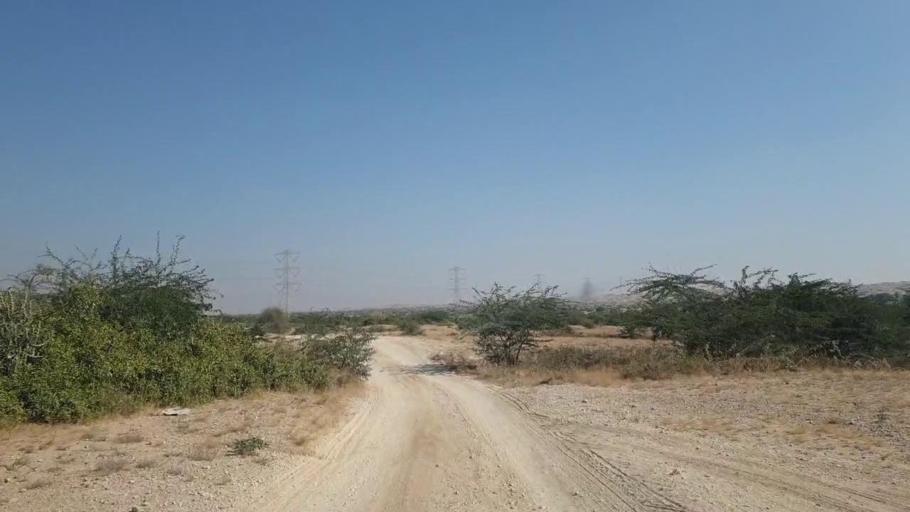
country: PK
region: Sindh
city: Gharo
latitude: 25.1938
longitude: 67.7415
